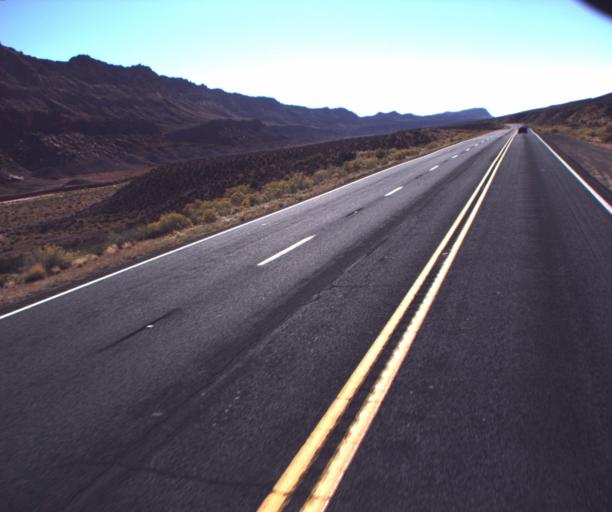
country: US
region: Arizona
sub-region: Coconino County
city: Tuba City
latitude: 36.2519
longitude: -111.4196
